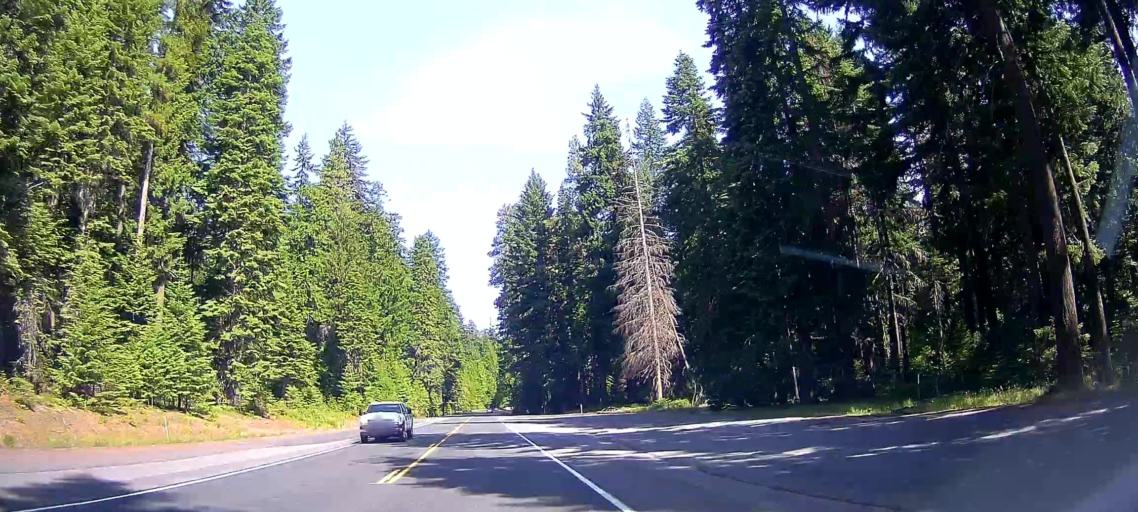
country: US
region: Oregon
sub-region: Jefferson County
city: Warm Springs
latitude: 45.0924
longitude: -121.5504
